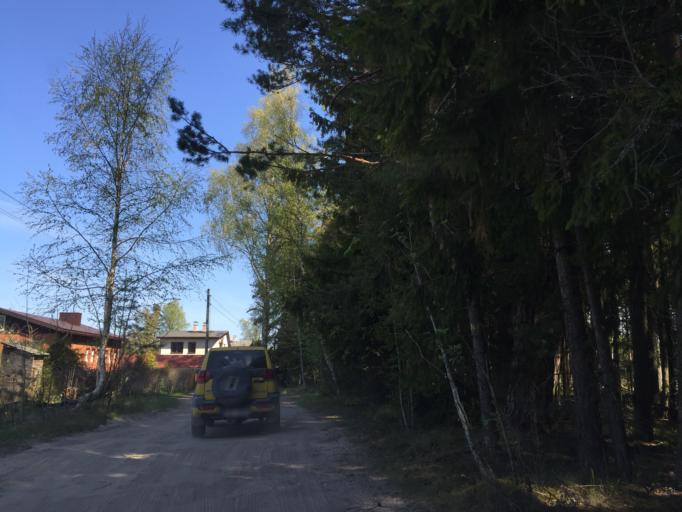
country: LV
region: Saulkrastu
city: Saulkrasti
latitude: 57.3172
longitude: 24.4384
